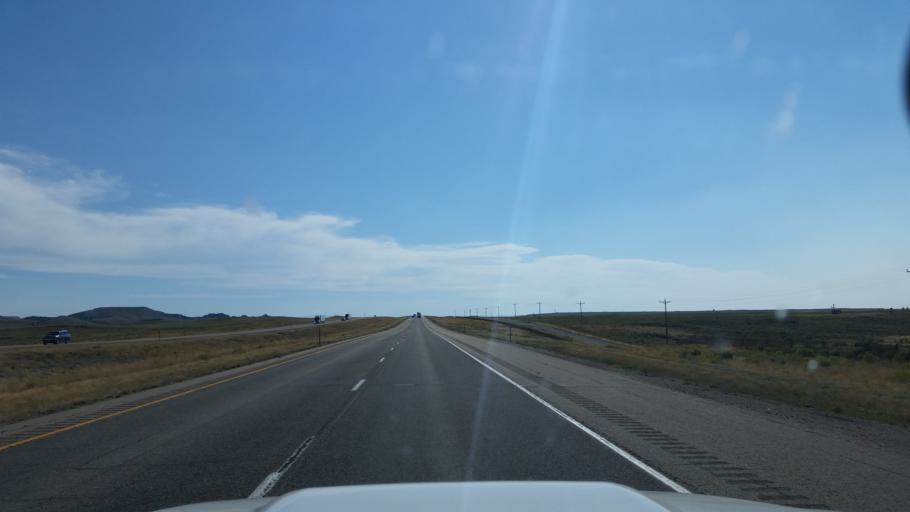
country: US
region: Wyoming
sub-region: Uinta County
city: Lyman
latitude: 41.4437
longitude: -110.0866
